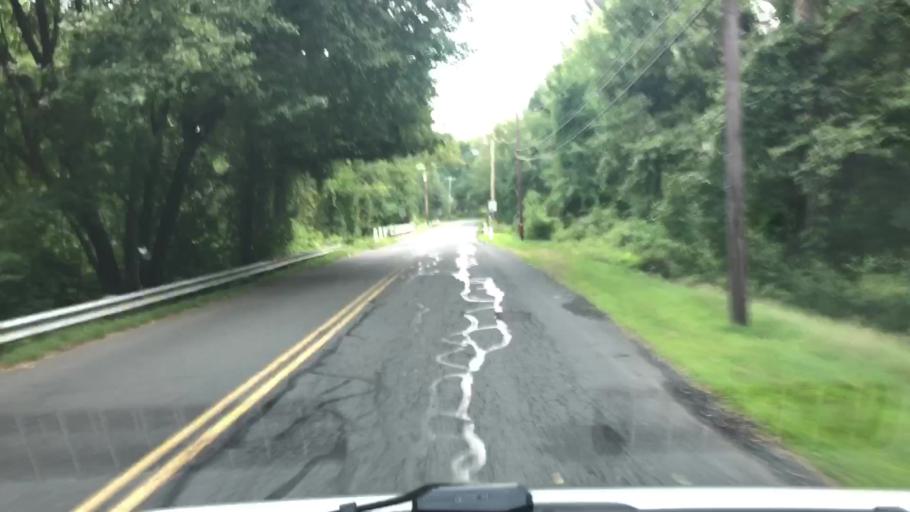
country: US
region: Massachusetts
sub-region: Hampshire County
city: Hatfield
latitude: 42.3802
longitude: -72.6261
